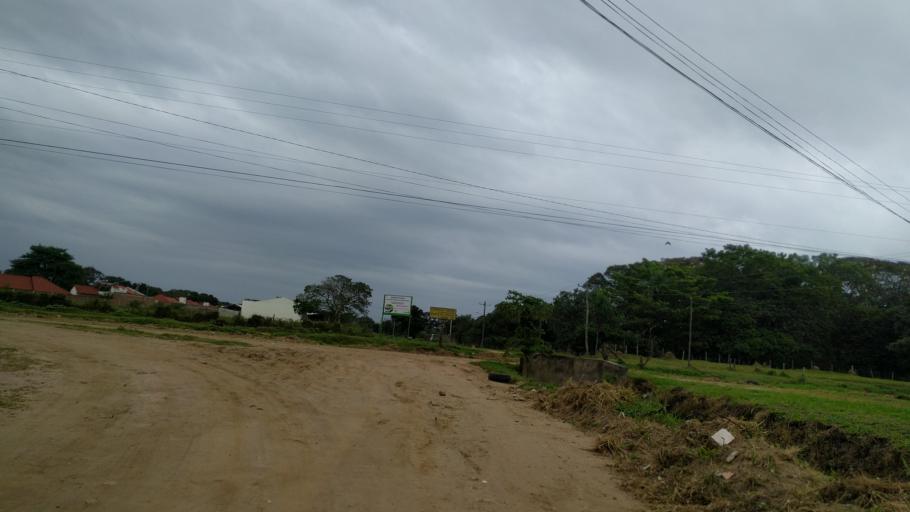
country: BO
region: Santa Cruz
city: Santa Cruz de la Sierra
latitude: -17.8106
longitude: -63.2324
